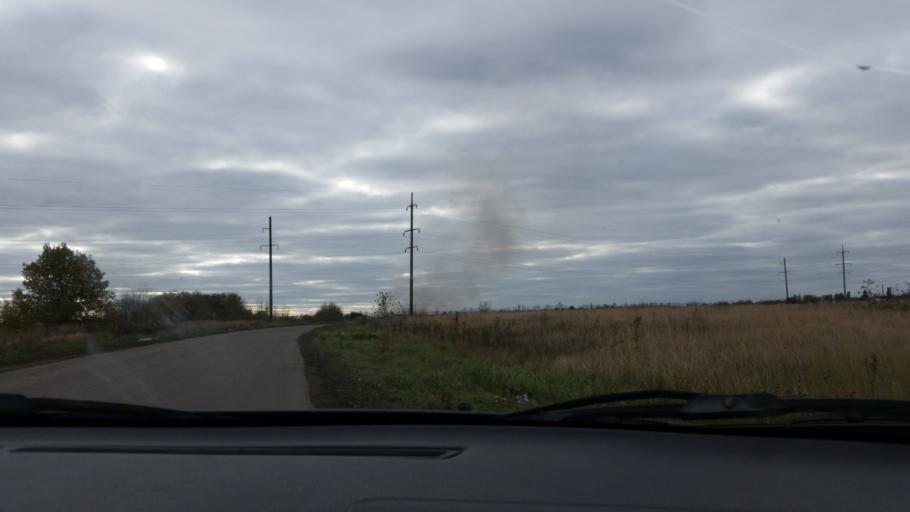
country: RU
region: Lipetsk
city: Gryazi
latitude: 52.4641
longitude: 39.9317
